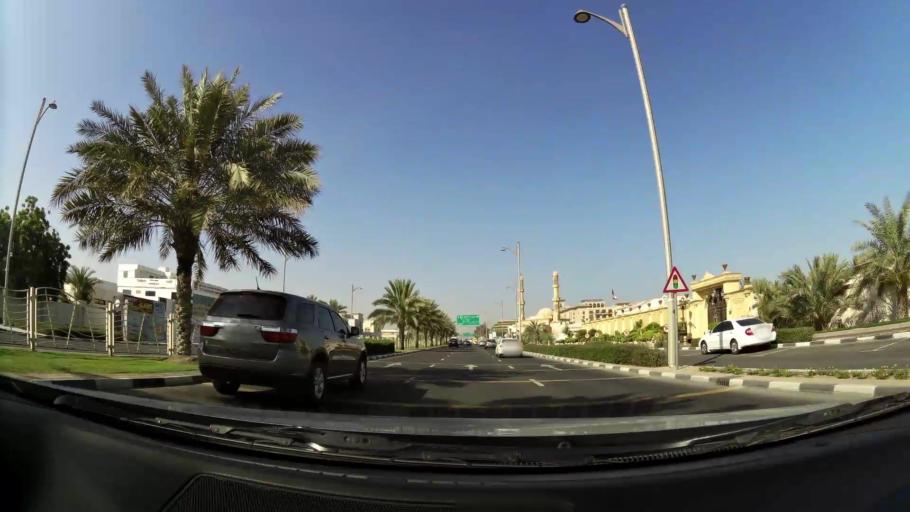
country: AE
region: Dubai
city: Dubai
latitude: 25.2051
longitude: 55.2429
